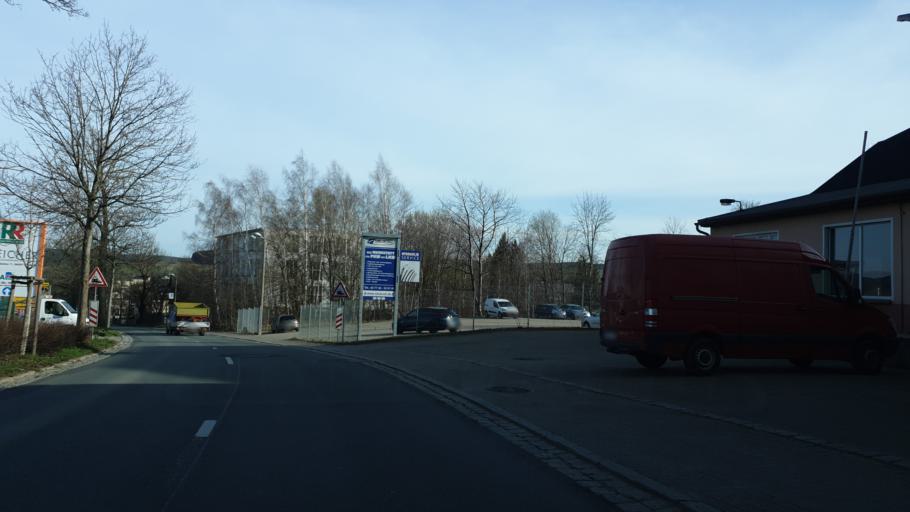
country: DE
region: Saxony
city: Zwonitz
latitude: 50.6339
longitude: 12.7947
